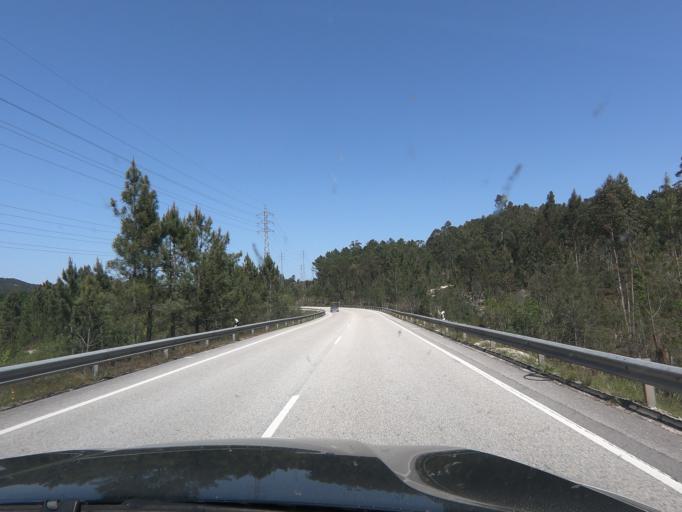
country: PT
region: Coimbra
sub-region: Miranda do Corvo
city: Miranda do Corvo
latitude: 40.0967
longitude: -8.3131
